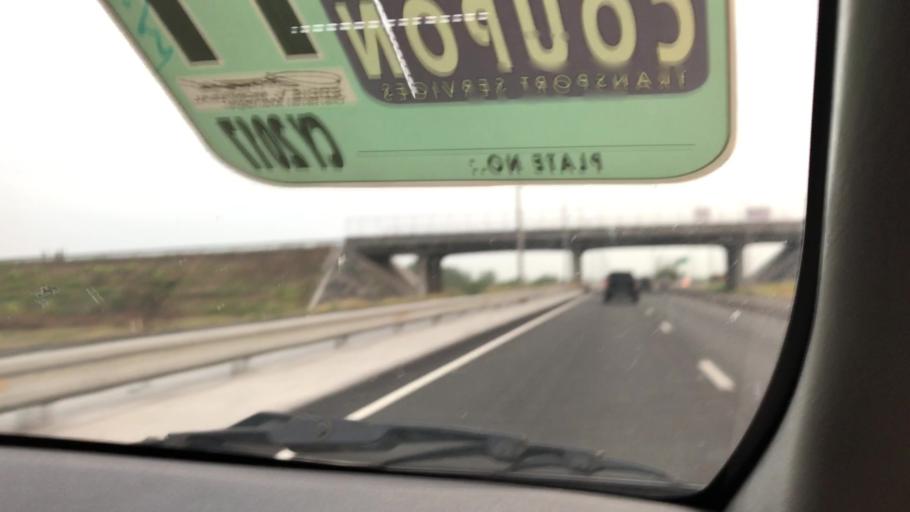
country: PH
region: Central Luzon
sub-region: Province of Tarlac
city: Mapalacsiao
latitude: 15.4331
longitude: 120.6657
